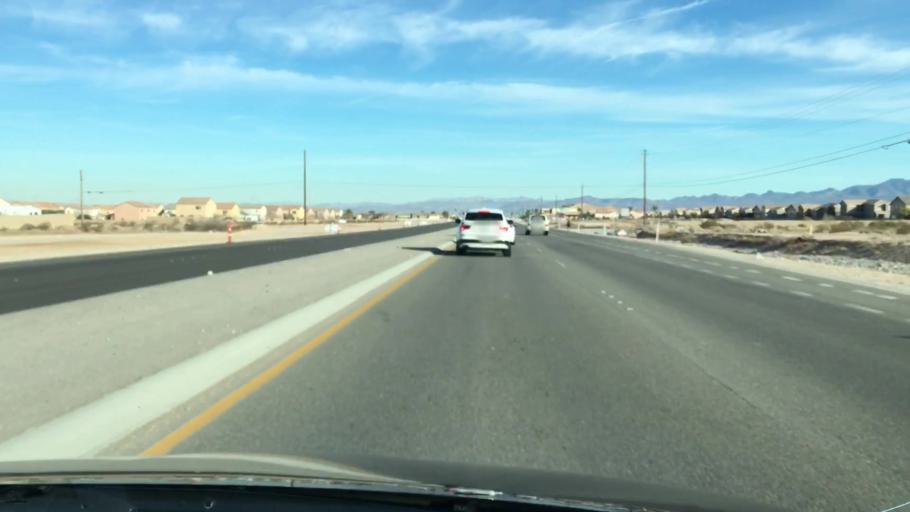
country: US
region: Nevada
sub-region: Clark County
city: Enterprise
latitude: 36.0204
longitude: -115.2950
